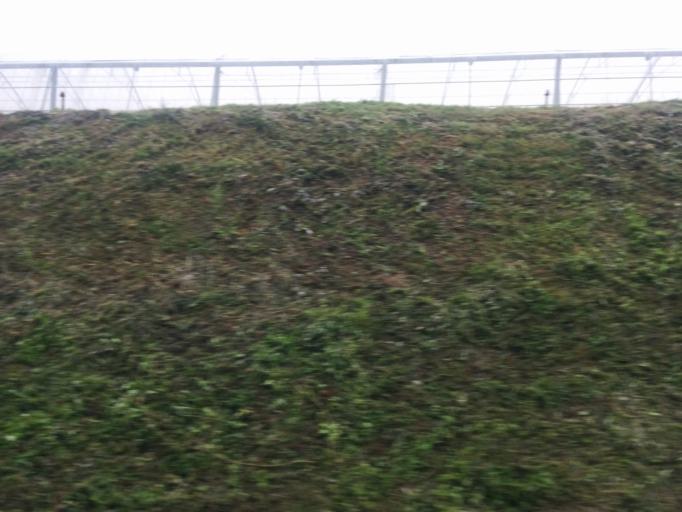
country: JP
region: Tochigi
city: Kanuma
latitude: 36.5854
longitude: 139.7551
